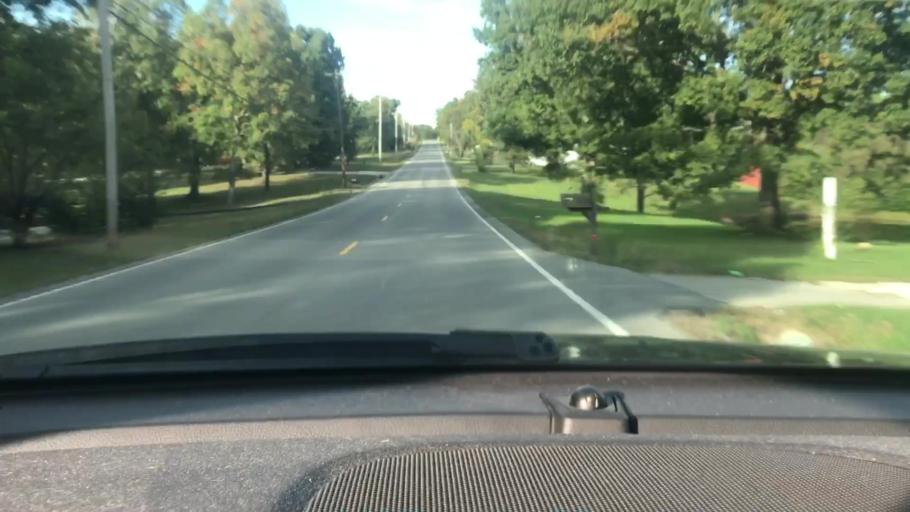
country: US
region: Tennessee
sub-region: Dickson County
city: White Bluff
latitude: 36.1427
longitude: -87.2354
